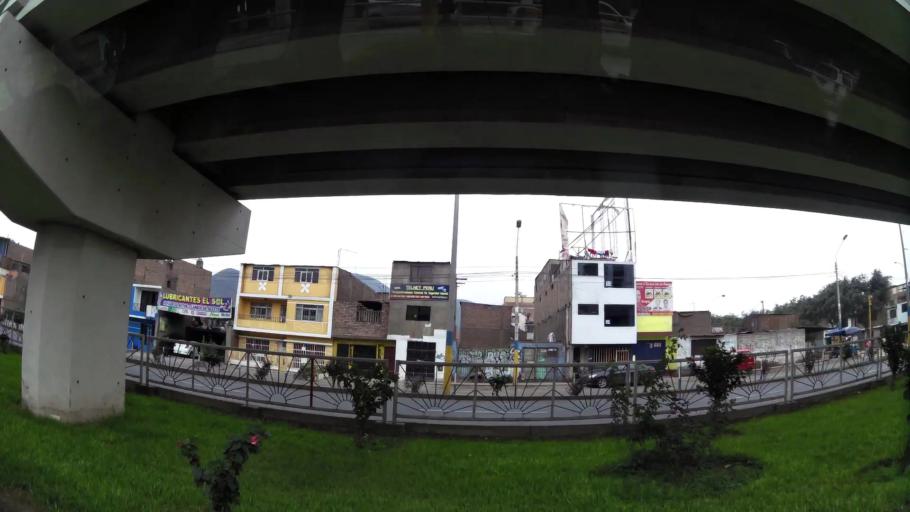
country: PE
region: Lima
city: Lima
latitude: -12.0236
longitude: -77.0080
